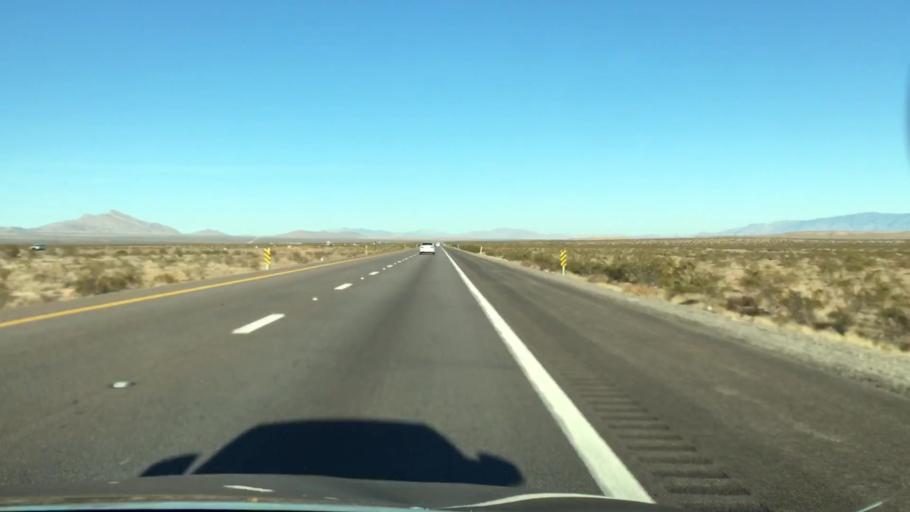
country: US
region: Nevada
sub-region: Clark County
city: Moapa Town
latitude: 36.7095
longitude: -114.4764
